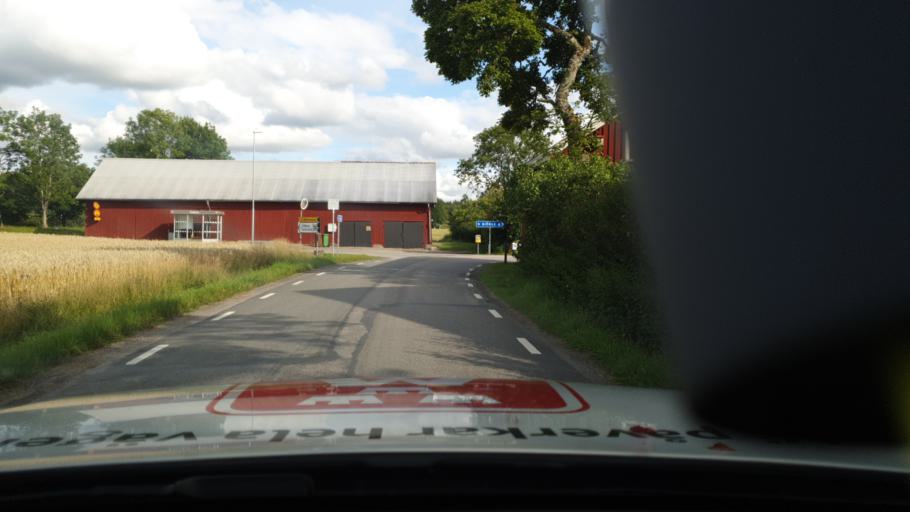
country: SE
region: Vaestra Goetaland
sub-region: Vanersborgs Kommun
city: Vargon
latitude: 58.2882
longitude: 12.5170
